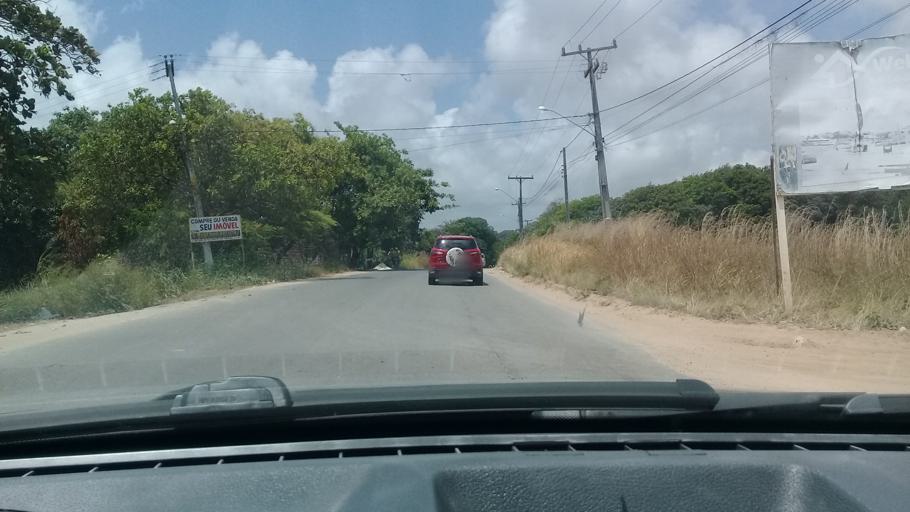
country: BR
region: Pernambuco
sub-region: Itamaraca
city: Itamaraca
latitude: -7.7823
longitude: -34.8372
